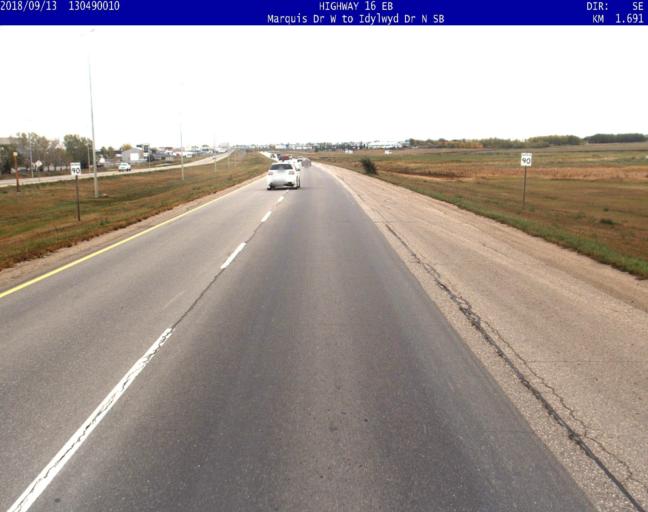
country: CA
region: Saskatchewan
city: Saskatoon
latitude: 52.1913
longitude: -106.6876
